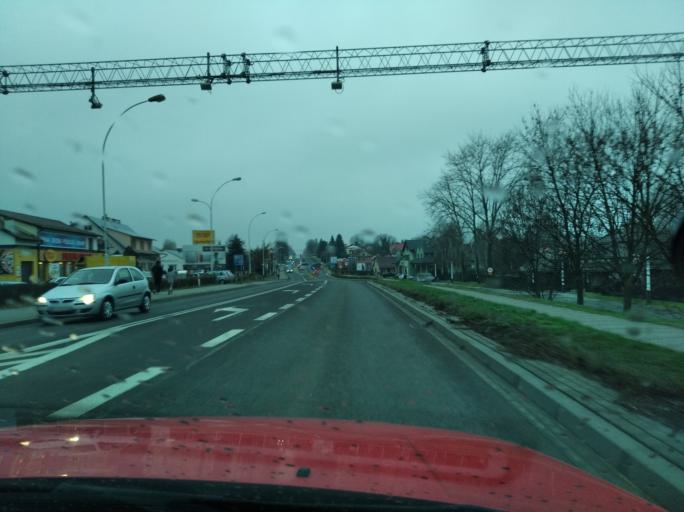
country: PL
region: Subcarpathian Voivodeship
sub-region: Powiat przeworski
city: Przeworsk
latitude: 50.0603
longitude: 22.4835
